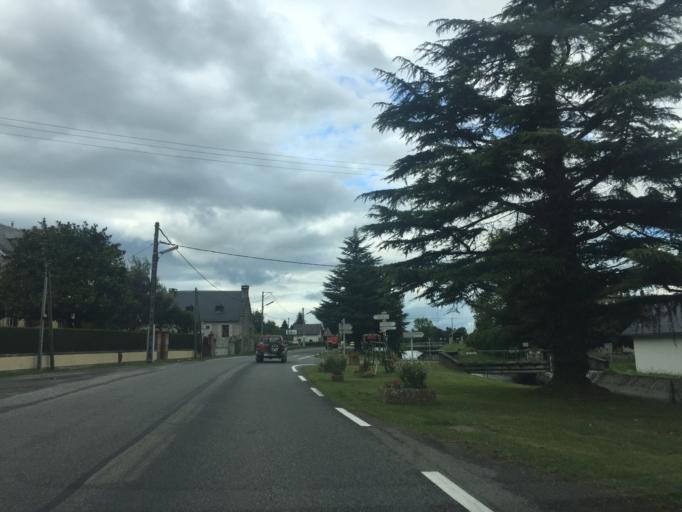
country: FR
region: Midi-Pyrenees
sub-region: Departement des Hautes-Pyrenees
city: La Barthe-de-Neste
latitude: 43.0203
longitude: 0.3722
